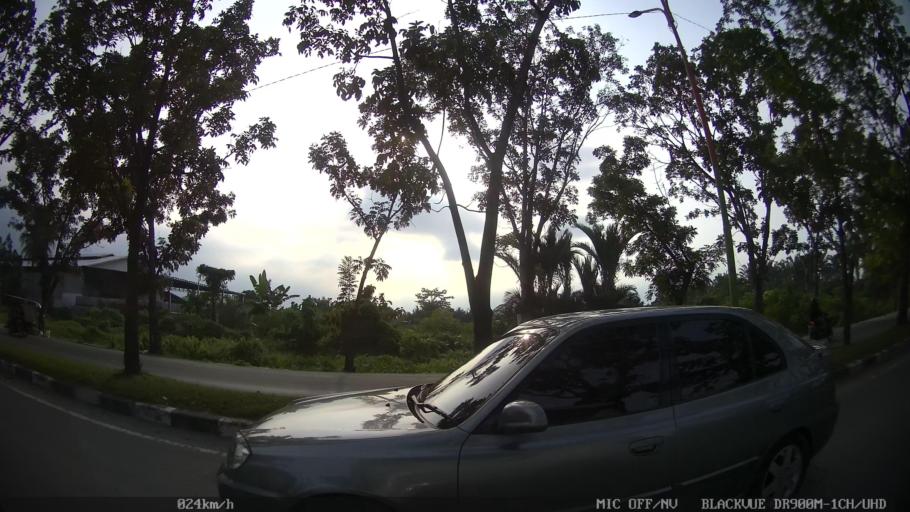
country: ID
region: North Sumatra
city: Binjai
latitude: 3.6082
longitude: 98.5341
